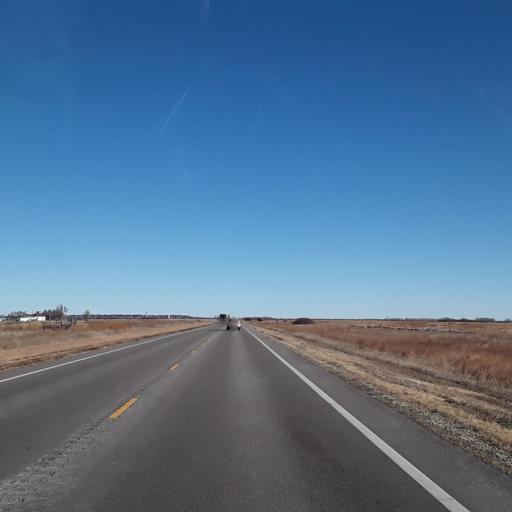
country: US
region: Kansas
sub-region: Pawnee County
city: Larned
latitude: 38.1371
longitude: -99.1546
